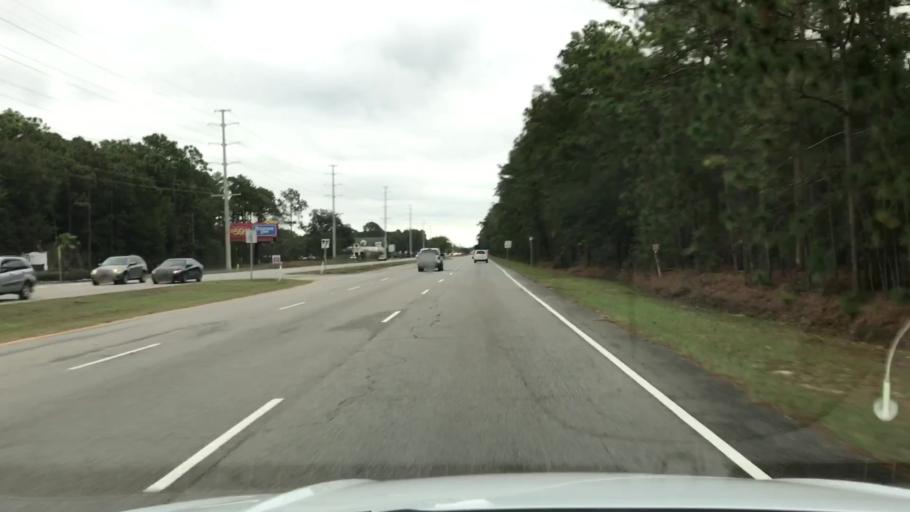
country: US
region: South Carolina
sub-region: Georgetown County
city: Georgetown
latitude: 33.4214
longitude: -79.1716
